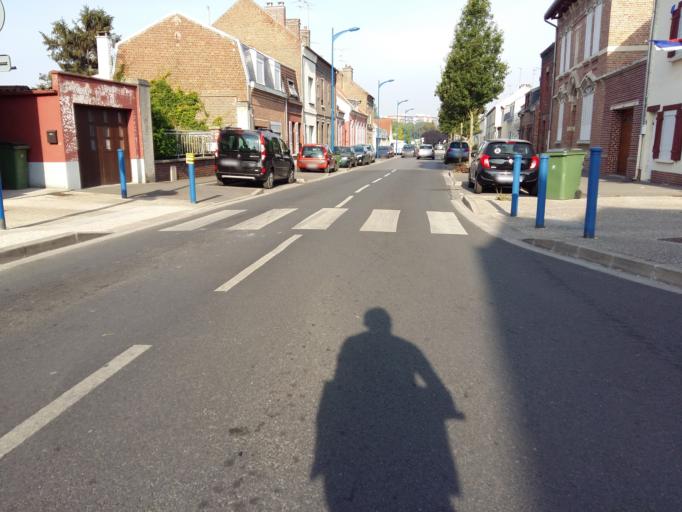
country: FR
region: Picardie
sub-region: Departement de la Somme
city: Rivery
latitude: 49.8992
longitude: 2.3224
